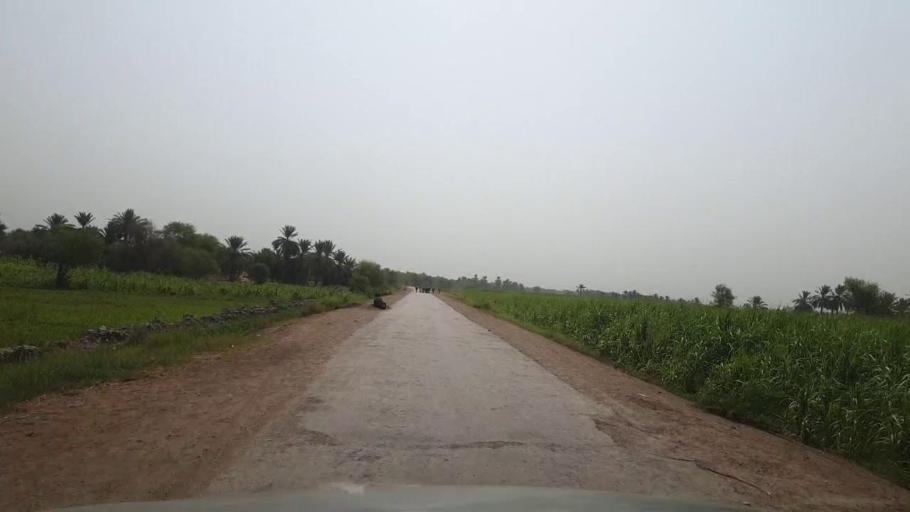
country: PK
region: Sindh
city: Gambat
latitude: 27.4313
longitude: 68.5217
